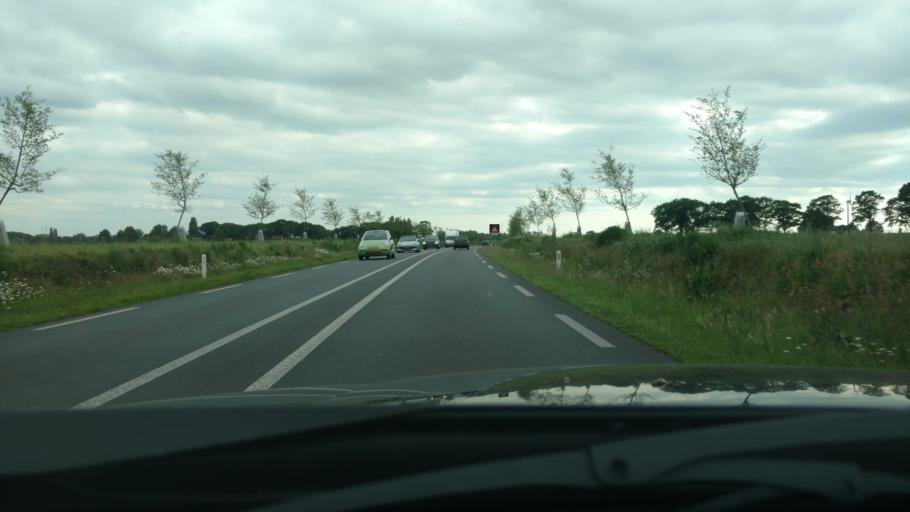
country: NL
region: Gelderland
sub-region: Gemeente Lochem
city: Eefde
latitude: 52.1713
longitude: 6.2128
